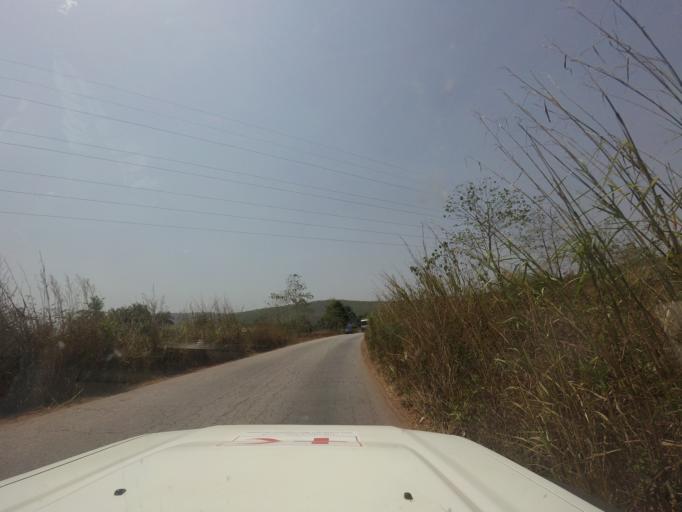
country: GN
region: Kindia
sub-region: Kindia
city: Kindia
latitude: 9.9090
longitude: -12.9956
